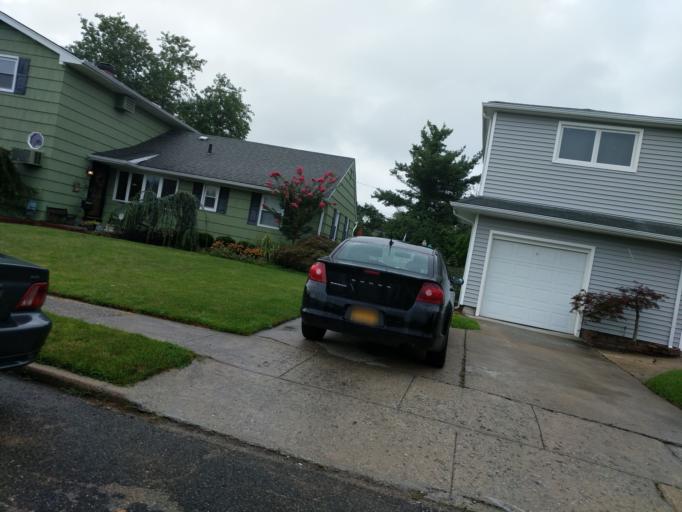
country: US
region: New York
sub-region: Nassau County
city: South Valley Stream
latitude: 40.6539
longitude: -73.7165
